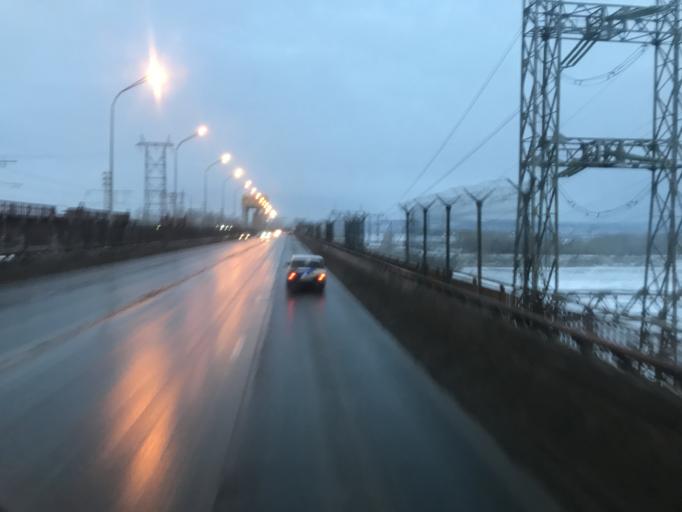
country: RU
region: Samara
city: Zhigulevsk
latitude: 53.4573
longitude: 49.4955
